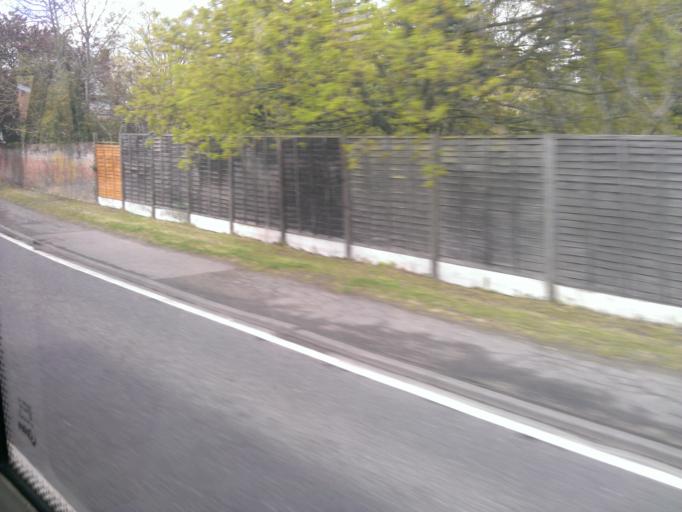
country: GB
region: England
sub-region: Essex
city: Eight Ash Green
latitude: 51.9069
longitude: 0.7914
